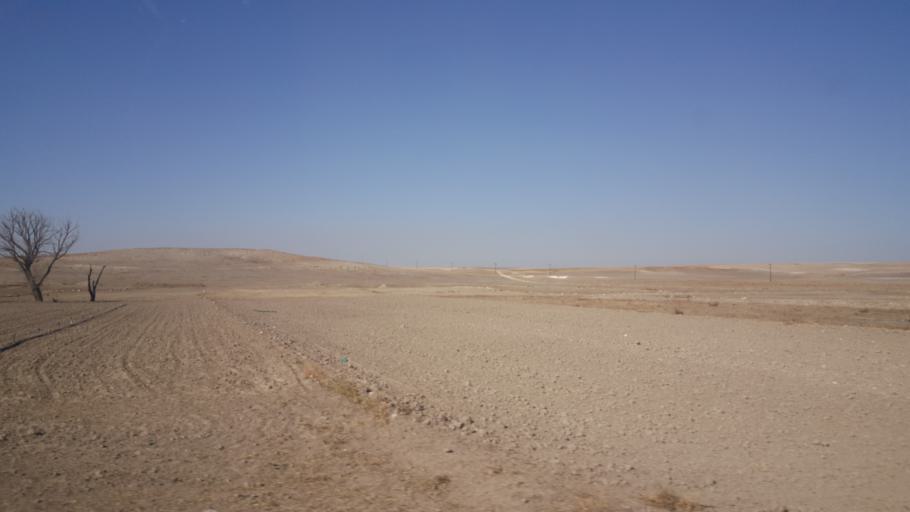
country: TR
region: Konya
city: Celtik
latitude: 39.0610
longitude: 31.8563
